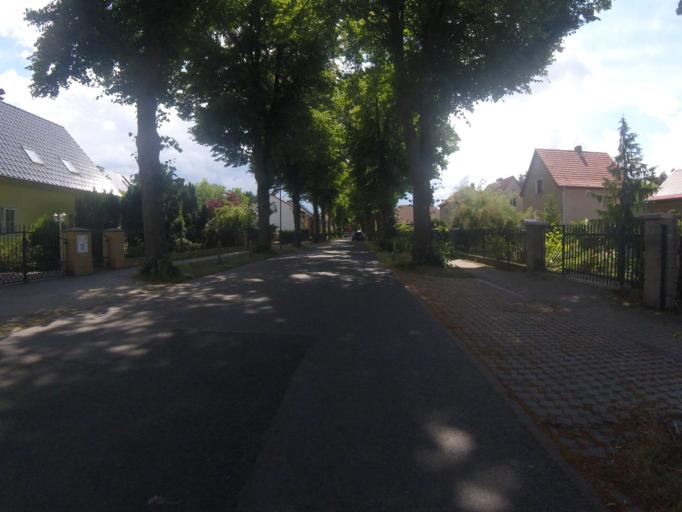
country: DE
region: Brandenburg
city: Konigs Wusterhausen
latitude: 52.2767
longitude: 13.6410
